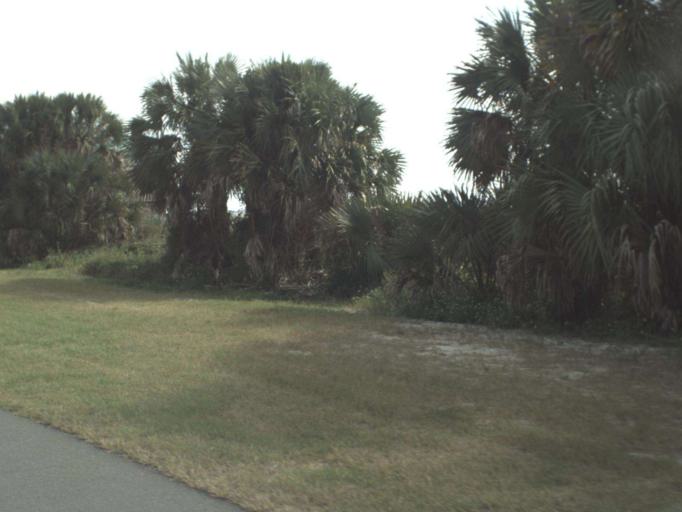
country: US
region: Florida
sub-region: Bay County
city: Mexico Beach
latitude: 29.9041
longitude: -85.3676
